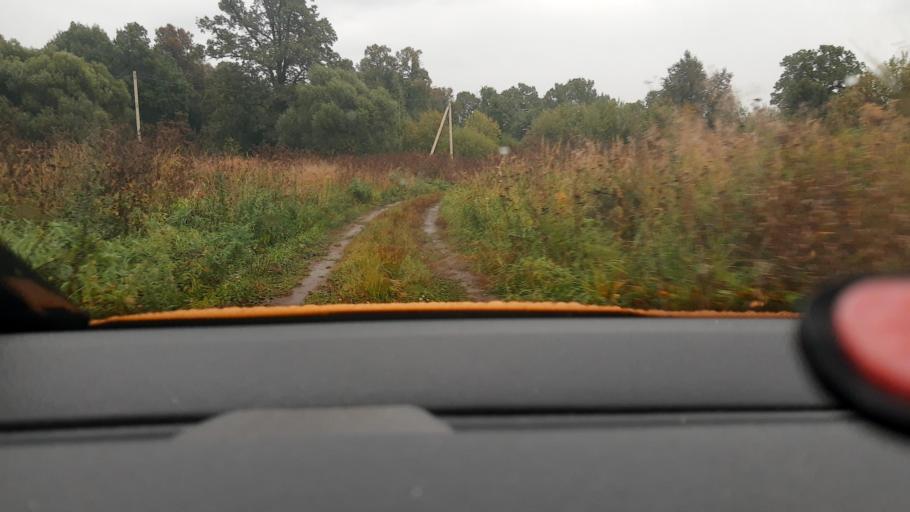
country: RU
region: Moskovskaya
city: Obukhovo
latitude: 55.8058
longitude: 38.2886
